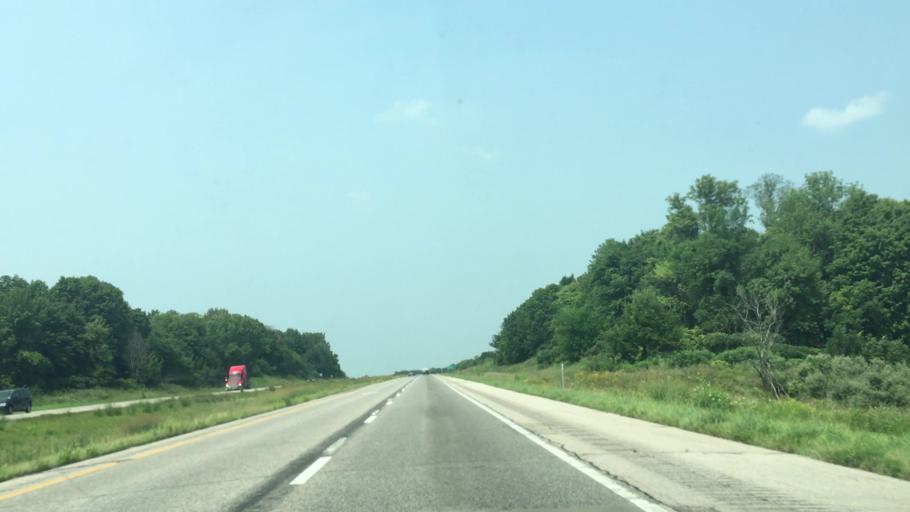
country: US
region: Iowa
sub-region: Benton County
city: Urbana
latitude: 42.2083
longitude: -91.8367
